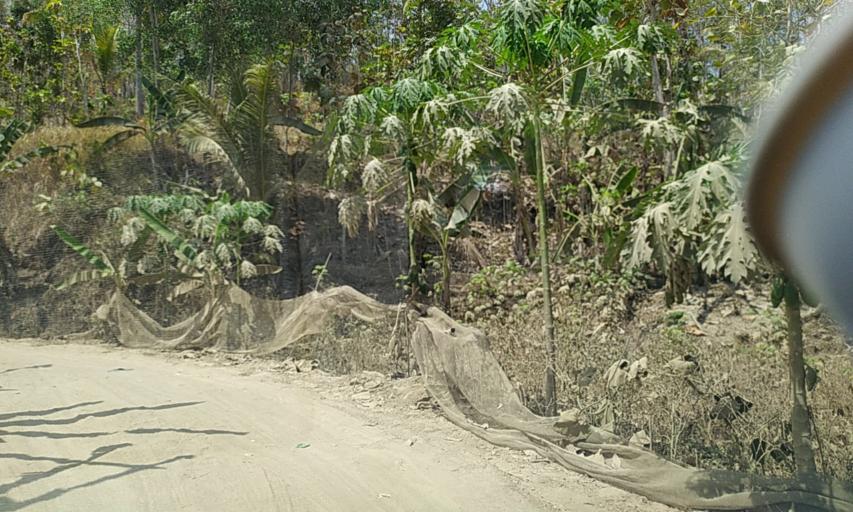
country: ID
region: Central Java
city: Karanggintung
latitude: -7.4647
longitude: 108.9102
